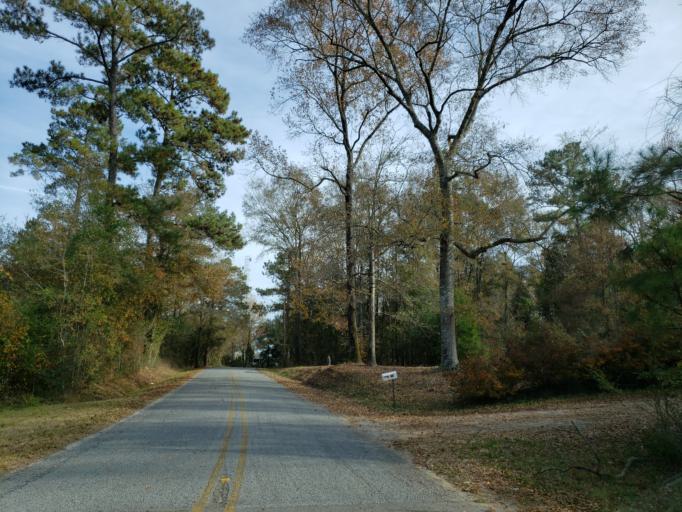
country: US
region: Mississippi
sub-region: Forrest County
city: Rawls Springs
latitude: 31.3782
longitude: -89.3697
